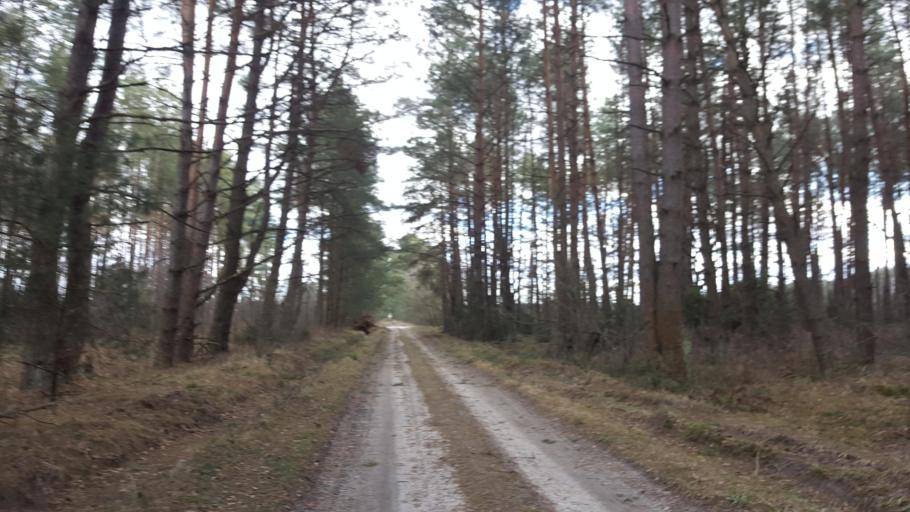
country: BY
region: Brest
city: Kamyanyets
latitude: 52.3938
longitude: 23.8691
